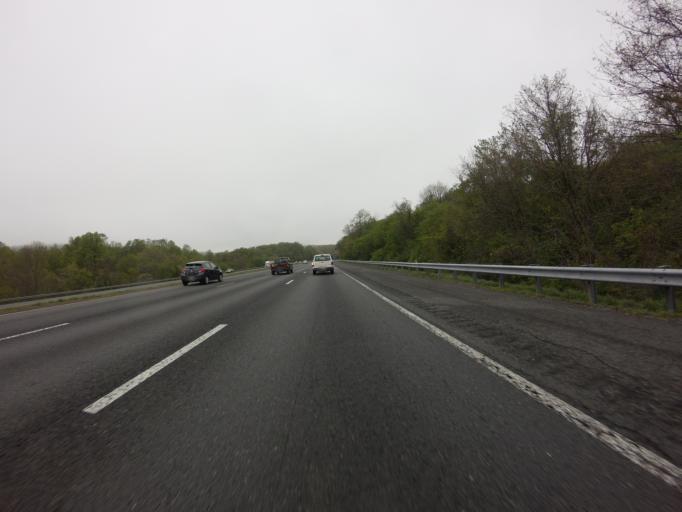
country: US
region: Maryland
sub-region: Frederick County
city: Myersville
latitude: 39.5200
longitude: -77.5990
